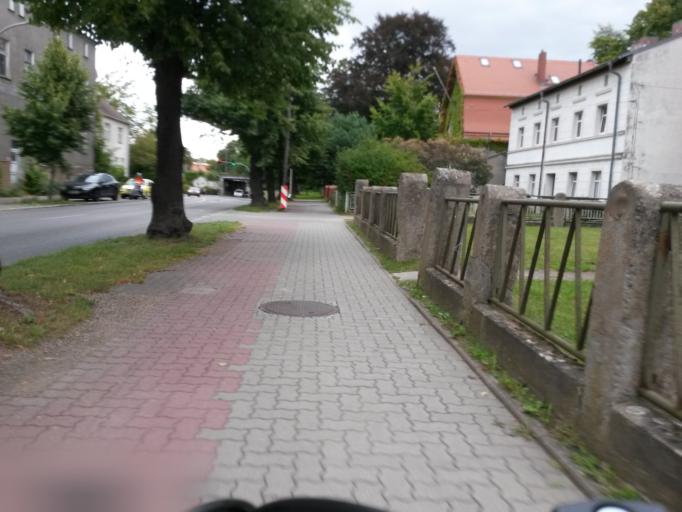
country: DE
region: Brandenburg
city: Angermunde
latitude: 53.0127
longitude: 13.9962
